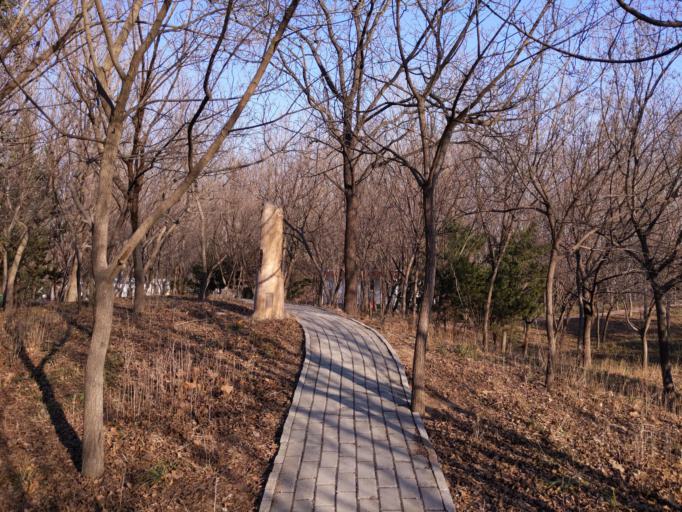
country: CN
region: Henan Sheng
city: Puyang
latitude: 35.7781
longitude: 114.9586
